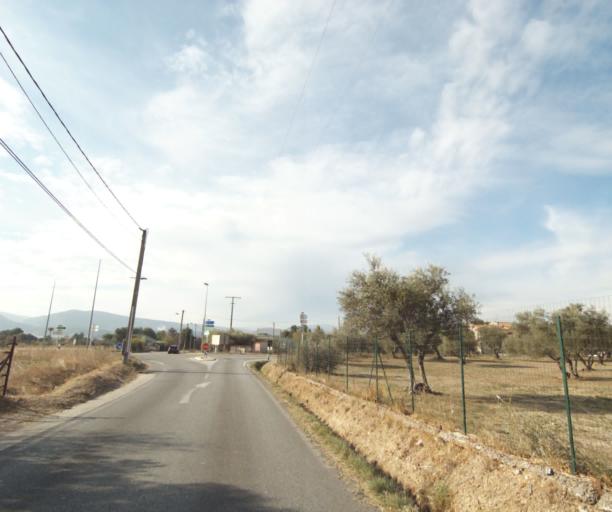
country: FR
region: Provence-Alpes-Cote d'Azur
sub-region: Departement des Bouches-du-Rhone
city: Gemenos
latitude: 43.3091
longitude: 5.6084
